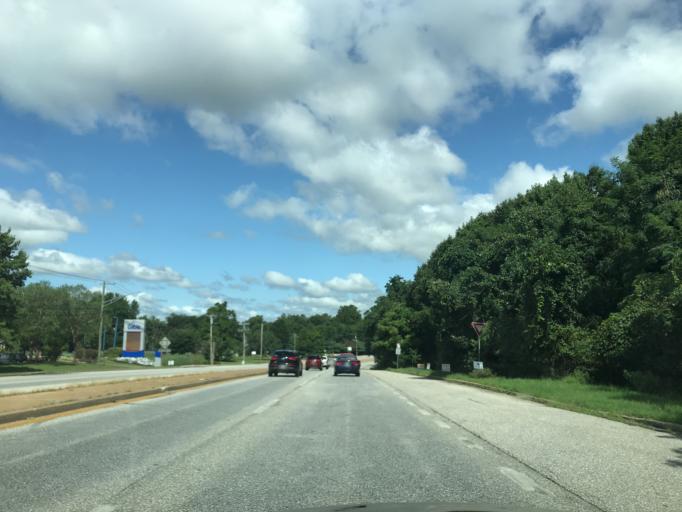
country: US
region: Maryland
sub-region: Anne Arundel County
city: Green Haven
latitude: 39.1816
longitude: -76.5485
